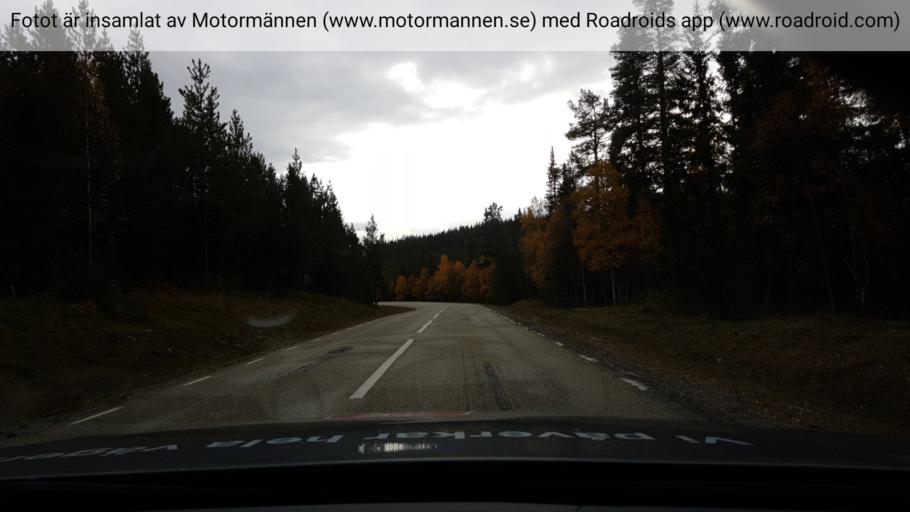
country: SE
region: Jaemtland
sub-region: Are Kommun
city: Are
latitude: 62.8188
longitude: 12.9230
